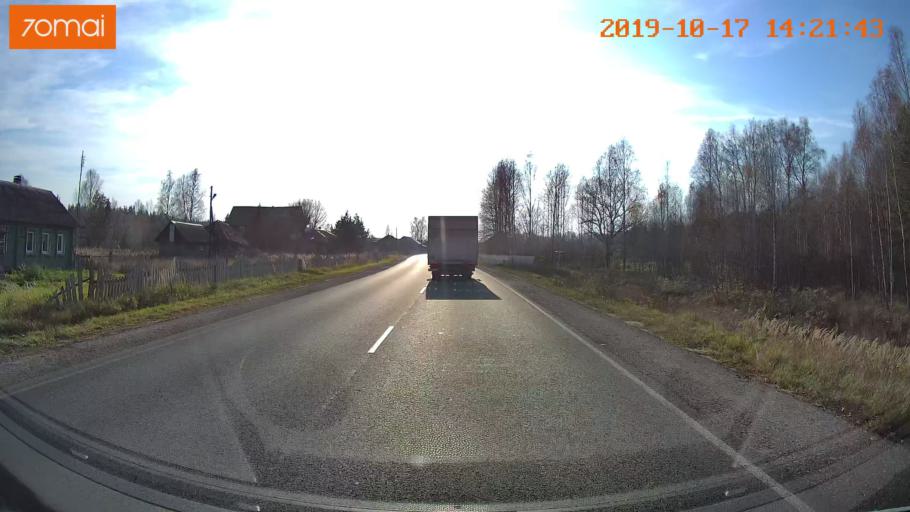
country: RU
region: Moskovskaya
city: Radovitskiy
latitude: 55.0357
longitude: 39.9753
